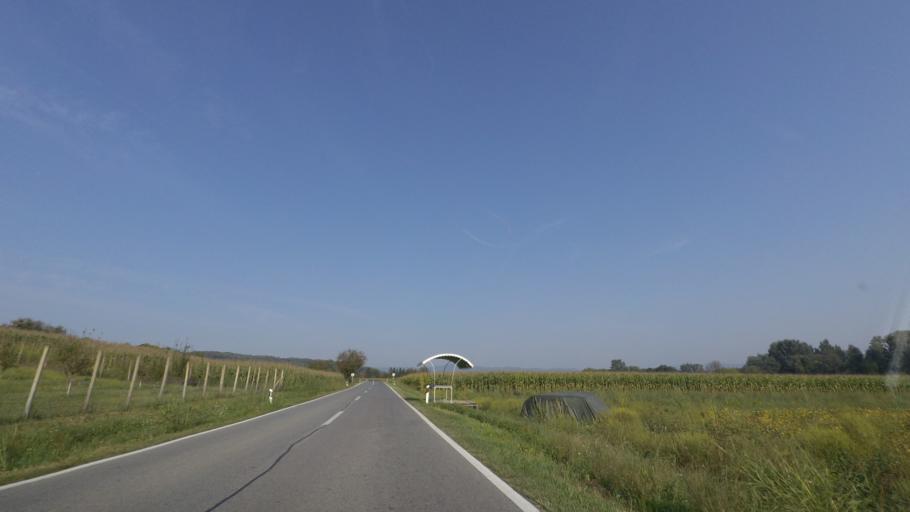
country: HR
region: Pozesko-Slavonska
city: Pozega
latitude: 45.3434
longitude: 17.5757
